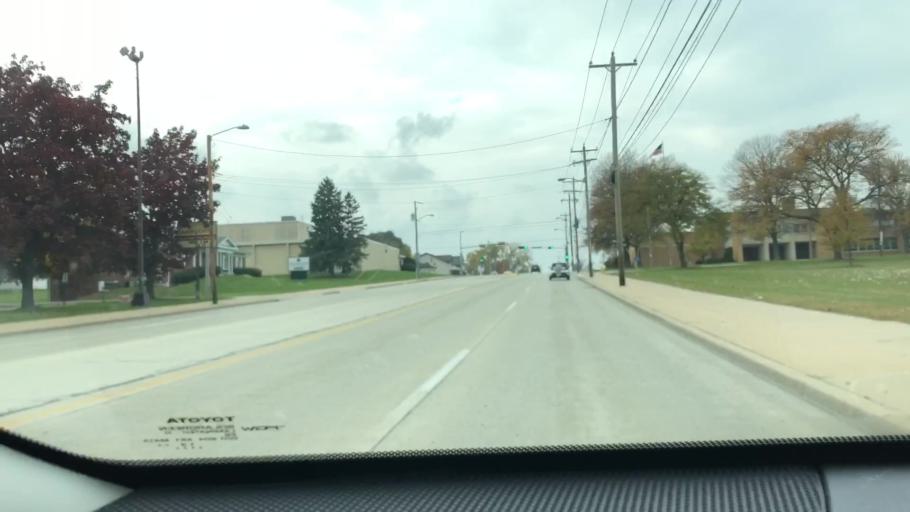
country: US
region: Wisconsin
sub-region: Brown County
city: Green Bay
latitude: 44.5190
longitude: -88.0503
